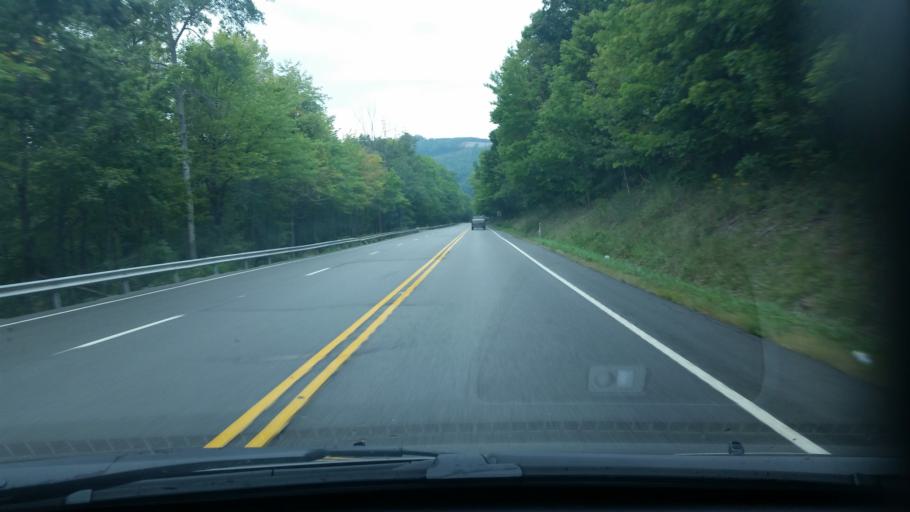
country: US
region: Pennsylvania
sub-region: Clearfield County
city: Shiloh
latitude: 41.0666
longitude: -78.3203
